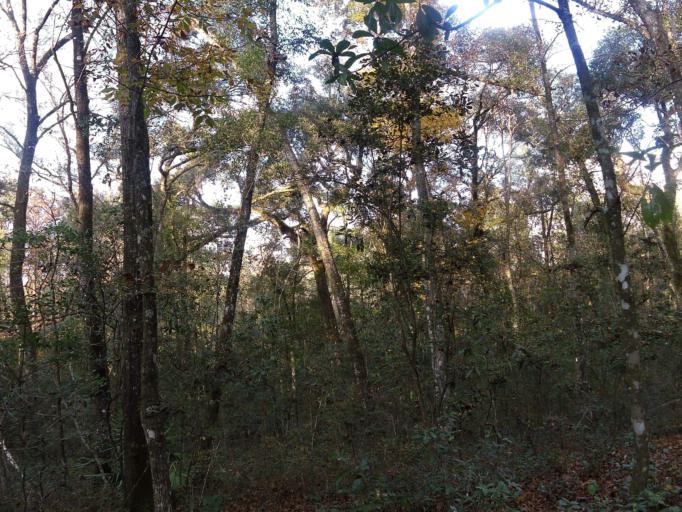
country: US
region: Florida
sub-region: Clay County
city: Middleburg
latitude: 30.1414
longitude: -81.9345
